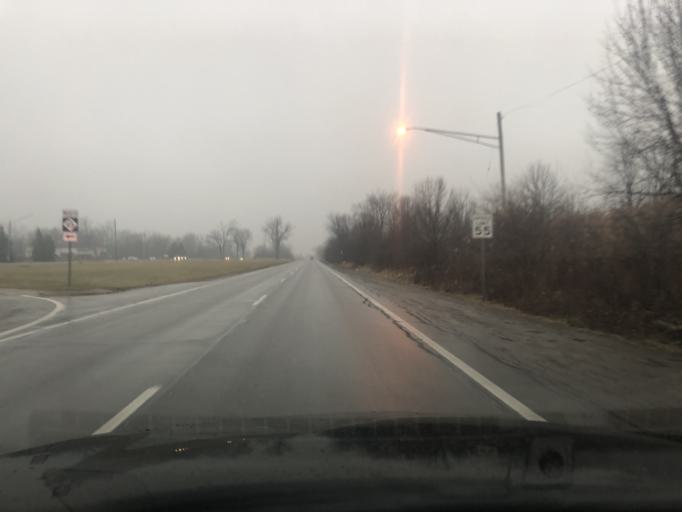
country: US
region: Michigan
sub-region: Wayne County
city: Gibraltar
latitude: 42.1109
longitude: -83.2162
